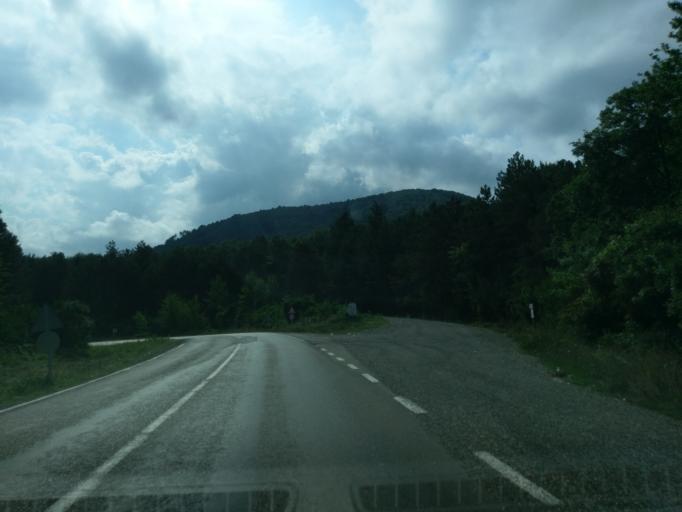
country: TR
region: Sinop
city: Yenikonak
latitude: 41.9413
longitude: 34.7094
